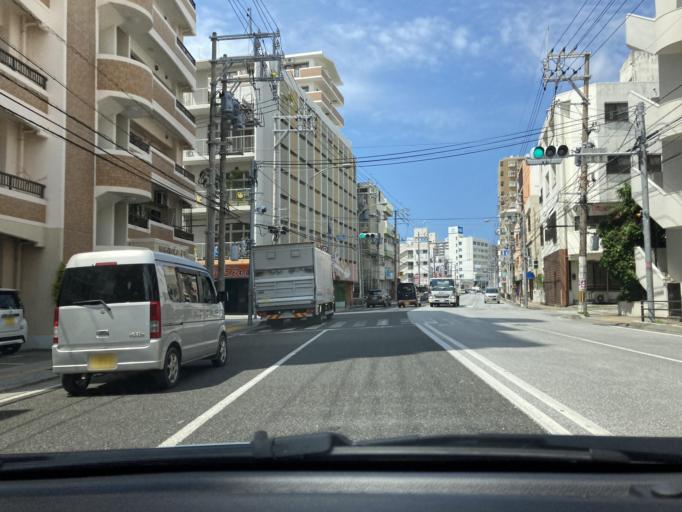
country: JP
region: Okinawa
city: Naha-shi
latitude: 26.2035
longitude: 127.6828
